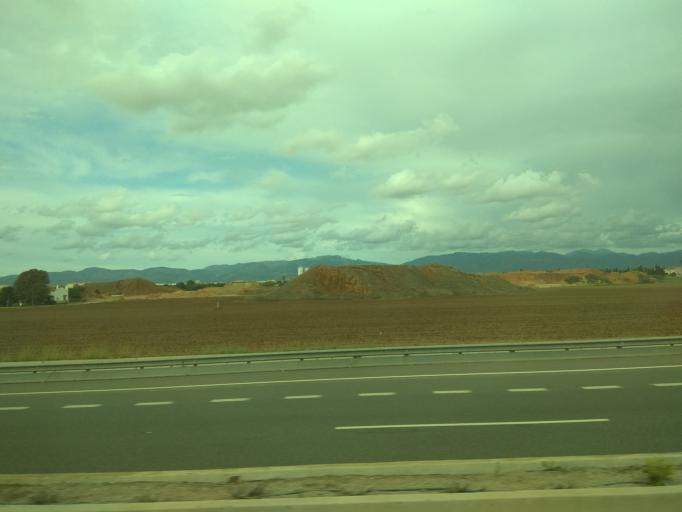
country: ES
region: Balearic Islands
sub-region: Illes Balears
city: Palma
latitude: 39.5698
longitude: 2.6976
